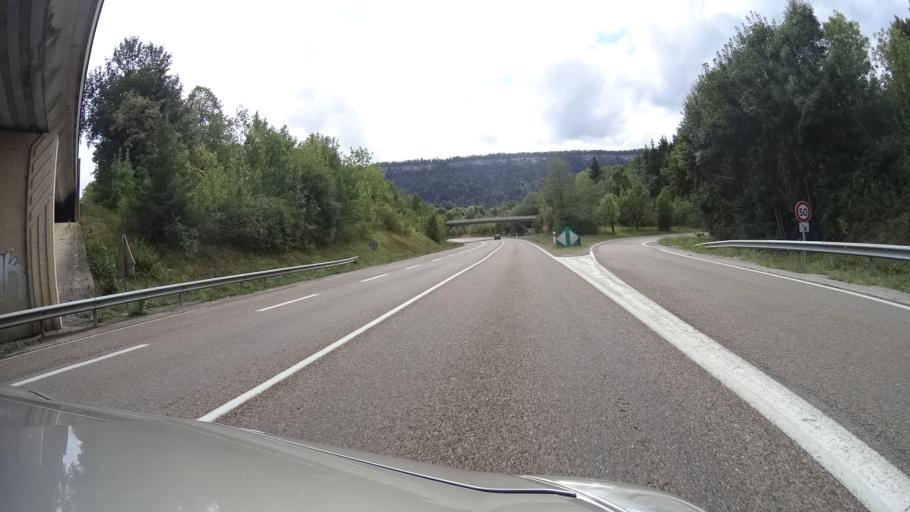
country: FR
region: Franche-Comte
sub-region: Departement du Jura
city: Champagnole
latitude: 46.7288
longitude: 5.9252
